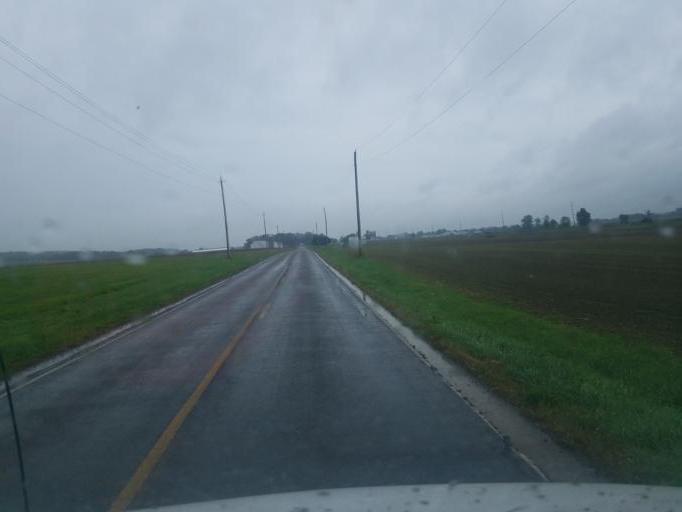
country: US
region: Ohio
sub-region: Medina County
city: Seville
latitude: 41.0038
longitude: -81.8596
